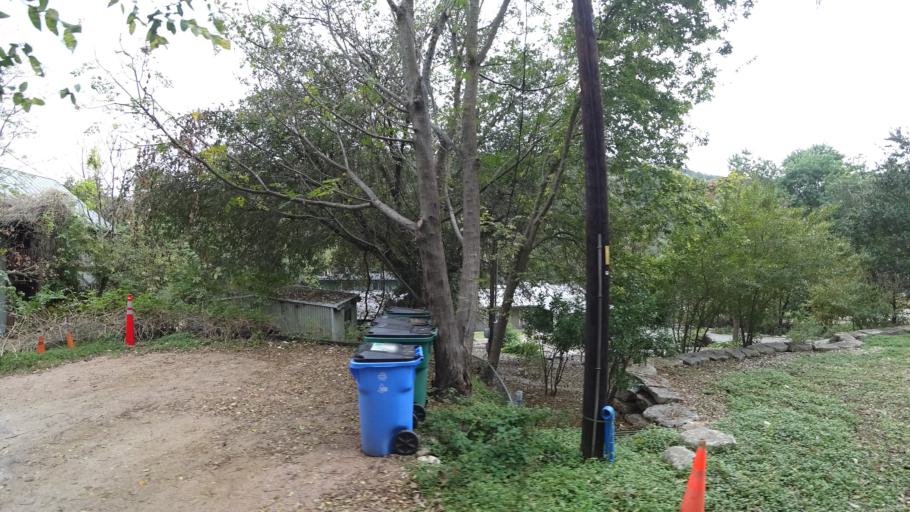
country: US
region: Texas
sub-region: Travis County
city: Bee Cave
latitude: 30.3297
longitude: -97.9303
